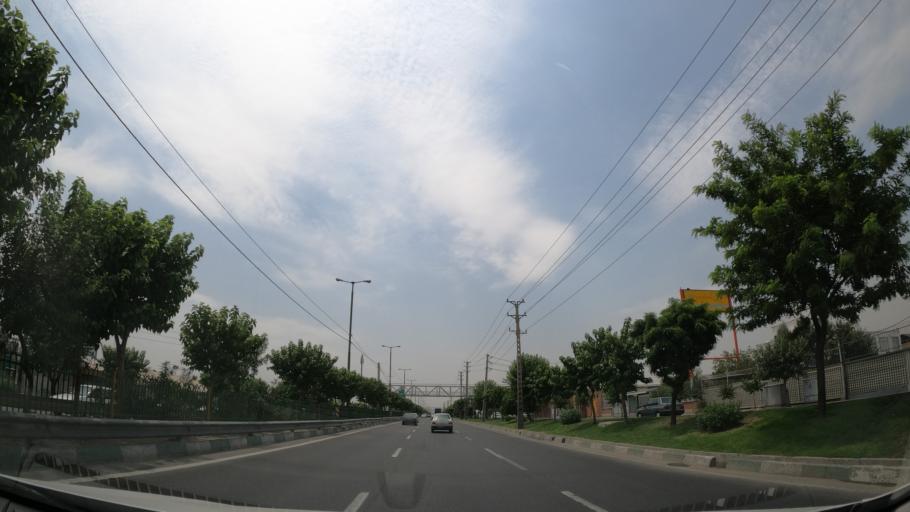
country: IR
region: Tehran
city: Tehran
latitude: 35.6764
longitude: 51.2899
